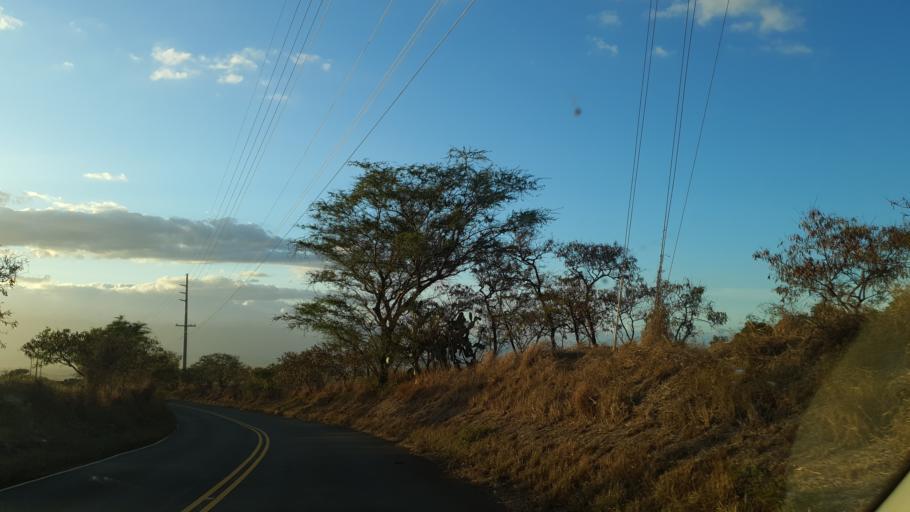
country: US
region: Hawaii
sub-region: Maui County
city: Pukalani
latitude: 20.7893
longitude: -156.3528
